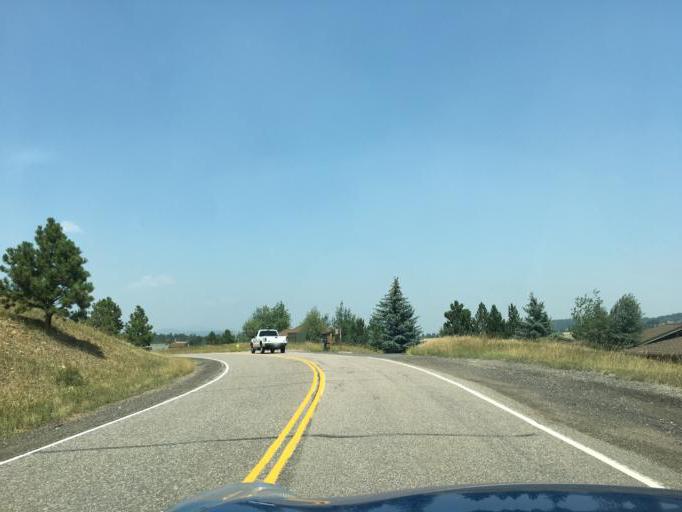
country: US
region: Colorado
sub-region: Jefferson County
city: Genesee
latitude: 39.6989
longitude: -105.2719
